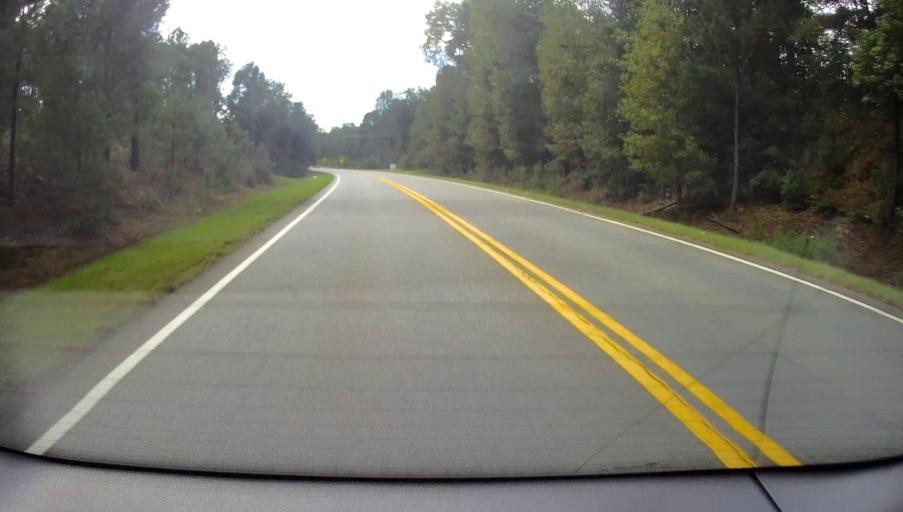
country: US
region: Georgia
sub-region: Jones County
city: Gray
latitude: 32.9832
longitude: -83.4145
